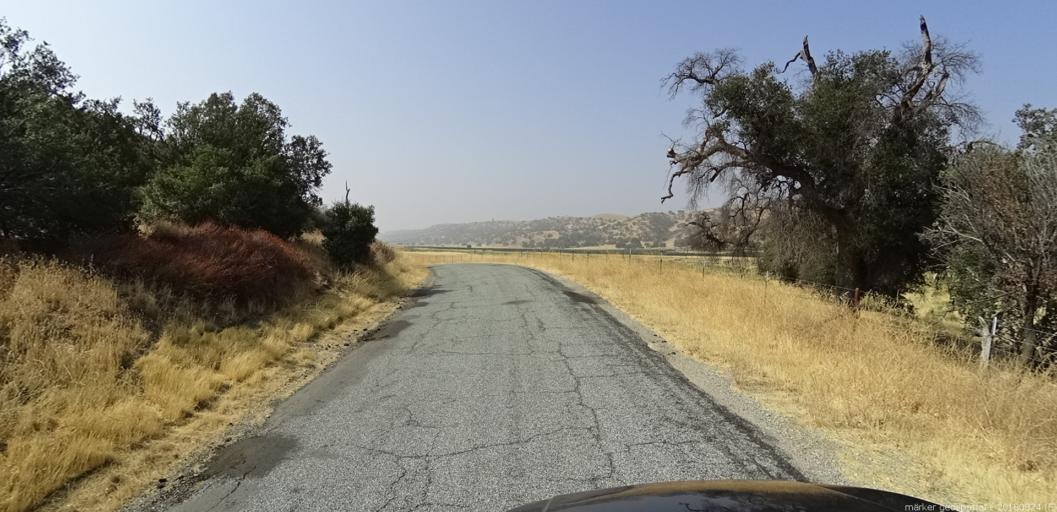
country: US
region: California
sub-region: San Luis Obispo County
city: San Miguel
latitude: 35.8997
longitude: -120.6976
